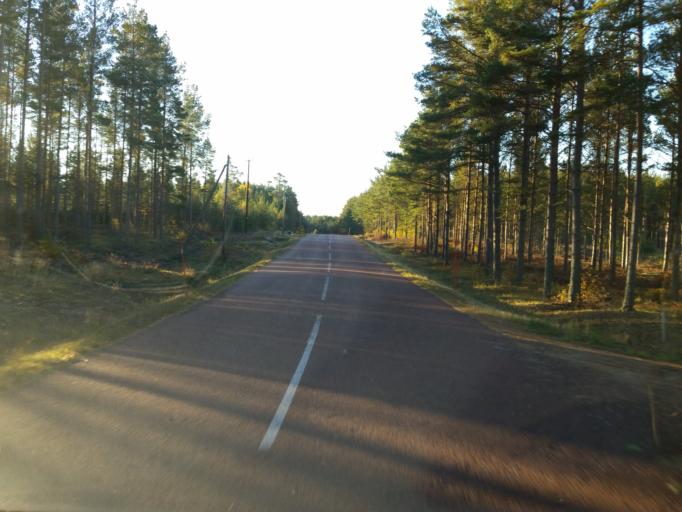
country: AX
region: Alands skaergard
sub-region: Vardoe
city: Vardoe
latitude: 60.2831
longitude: 20.3883
